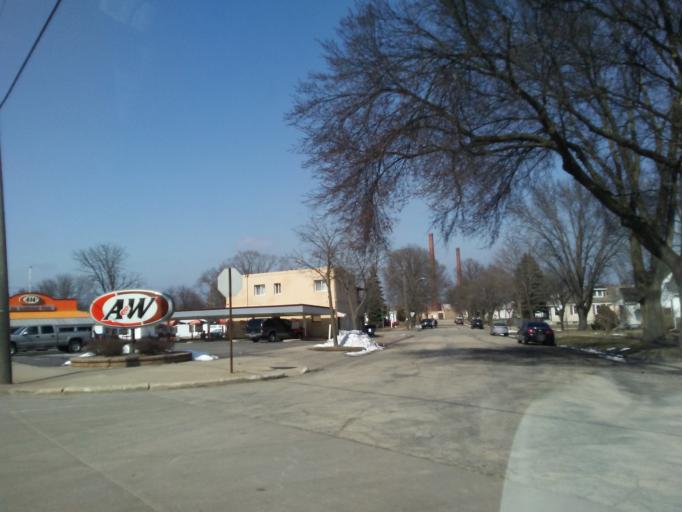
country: US
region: Wisconsin
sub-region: La Crosse County
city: La Crosse
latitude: 43.7843
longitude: -91.2307
